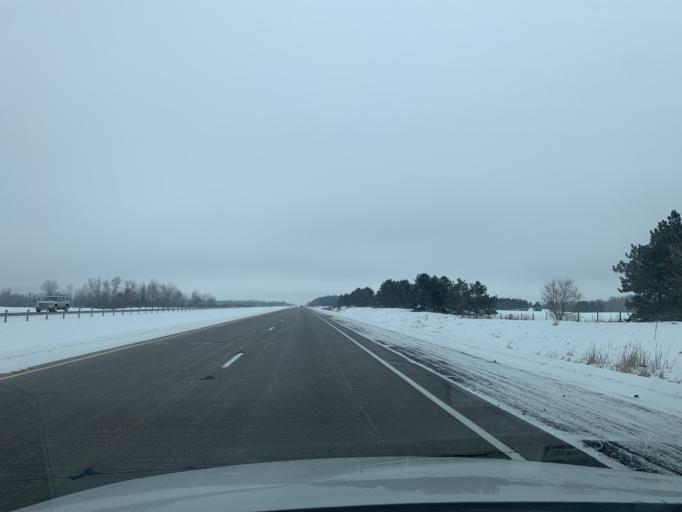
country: US
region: Minnesota
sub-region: Chisago County
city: Harris
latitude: 45.6184
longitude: -92.9921
